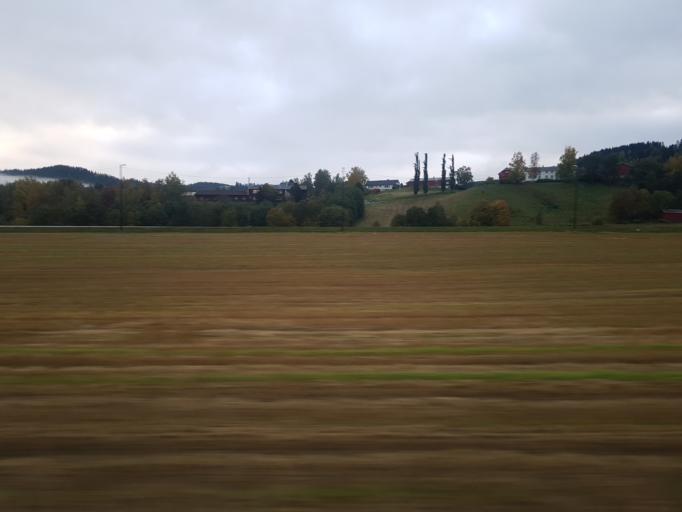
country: NO
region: Sor-Trondelag
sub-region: Melhus
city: Lundamo
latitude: 63.1328
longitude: 10.2541
